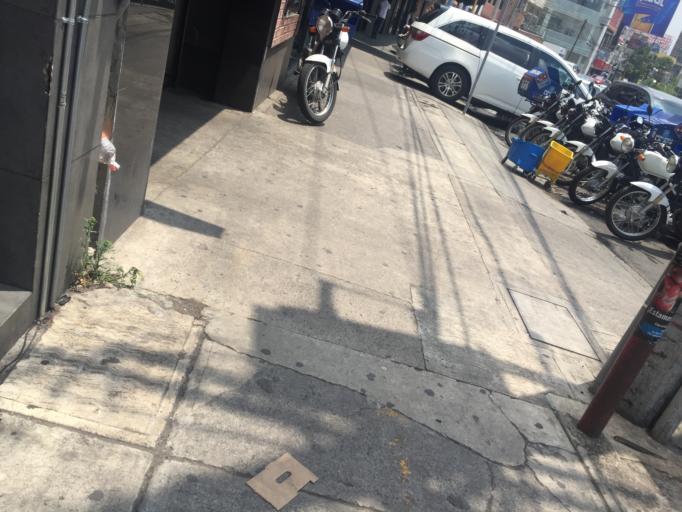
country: MX
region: Mexico City
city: Col. Bosques de las Lomas
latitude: 19.3899
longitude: -99.2603
